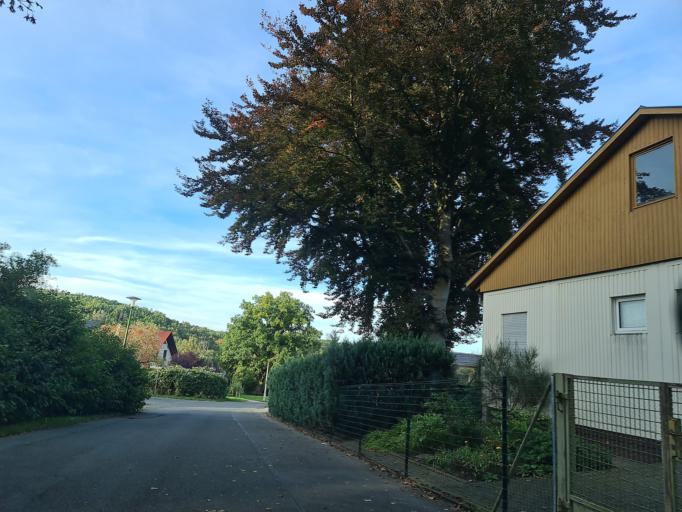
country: DE
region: Saxony
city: Plauen
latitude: 50.4983
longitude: 12.1163
